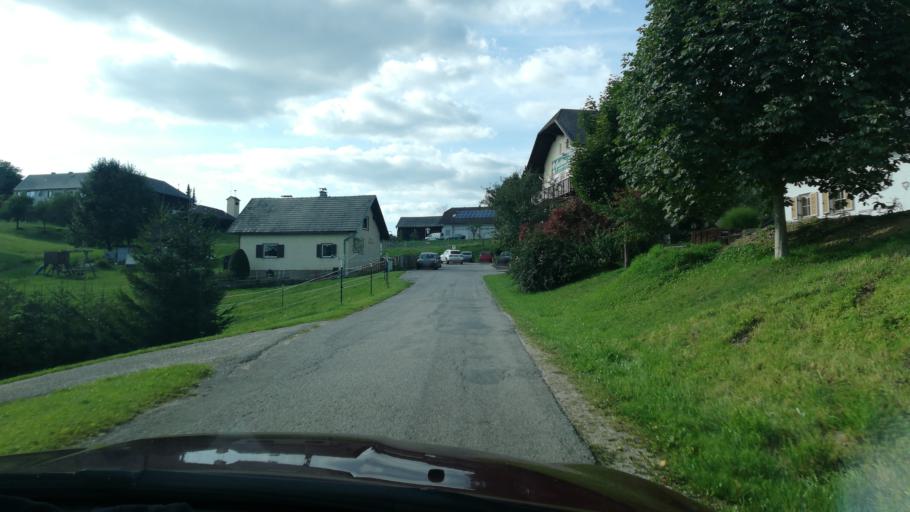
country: AT
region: Lower Austria
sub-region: Politischer Bezirk Zwettl
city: Langschlag
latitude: 48.4771
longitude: 14.8157
